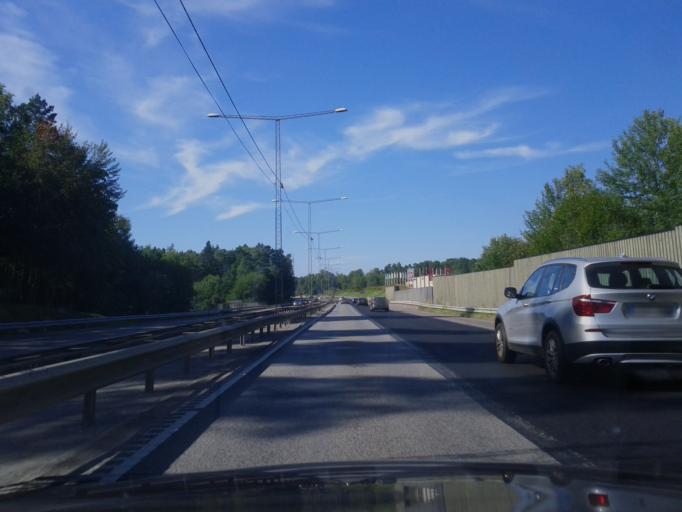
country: SE
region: Stockholm
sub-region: Danderyds Kommun
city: Djursholm
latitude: 59.4222
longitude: 18.0516
